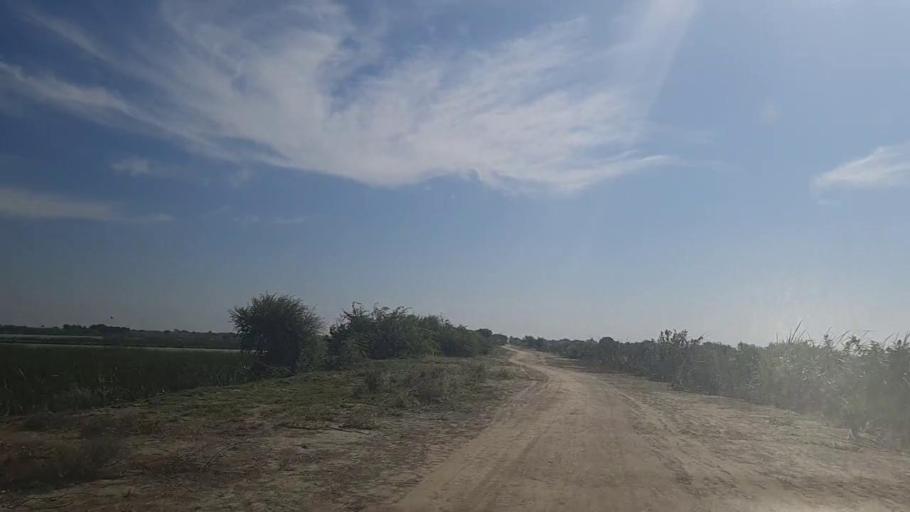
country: PK
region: Sindh
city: Mirpur Batoro
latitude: 24.6586
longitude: 68.1960
